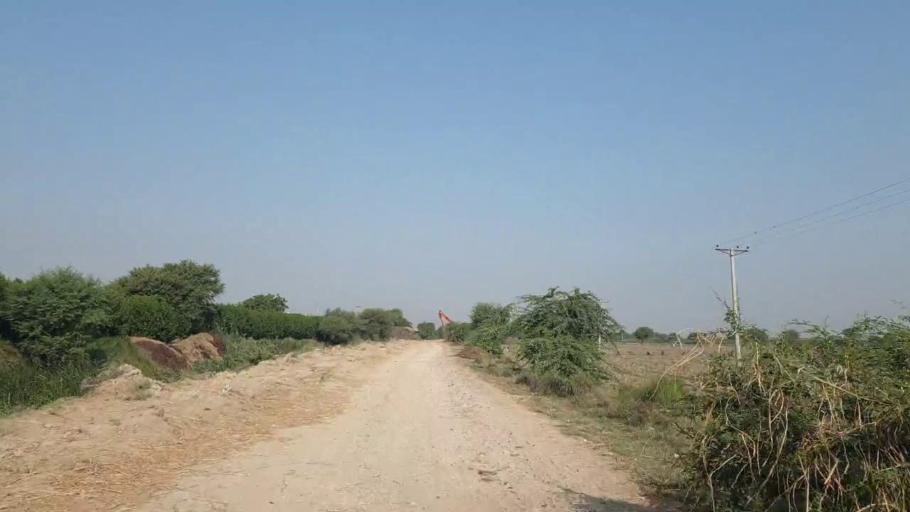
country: PK
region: Sindh
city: Matli
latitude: 24.9908
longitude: 68.6225
